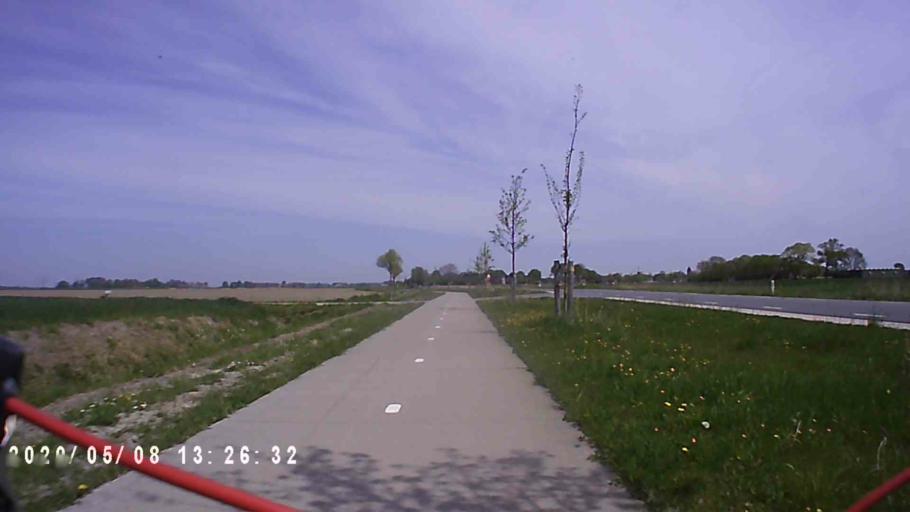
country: NL
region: Groningen
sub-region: Gemeente Bedum
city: Bedum
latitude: 53.3276
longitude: 6.7247
